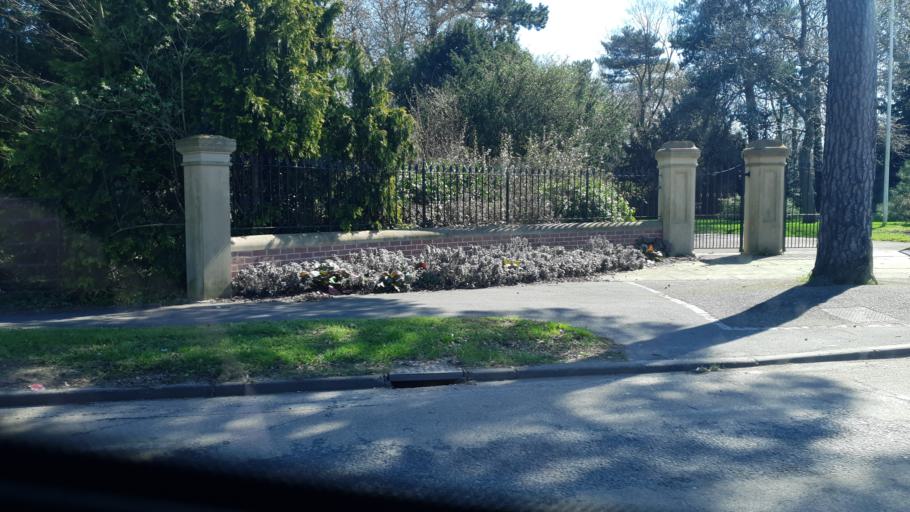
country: GB
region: England
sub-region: Middlesbrough
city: Nunthorpe
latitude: 54.5408
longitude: -1.2104
